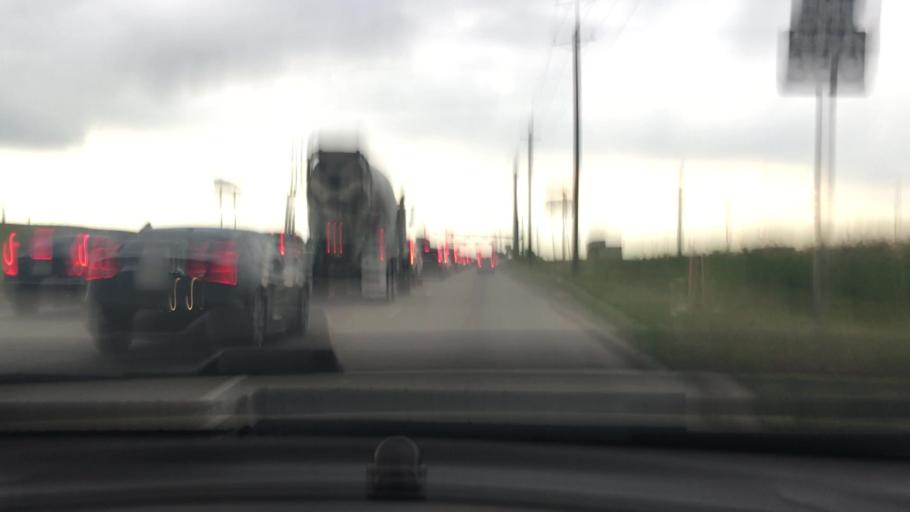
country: US
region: Texas
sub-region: Collin County
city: Prosper
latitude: 33.2171
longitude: -96.8195
